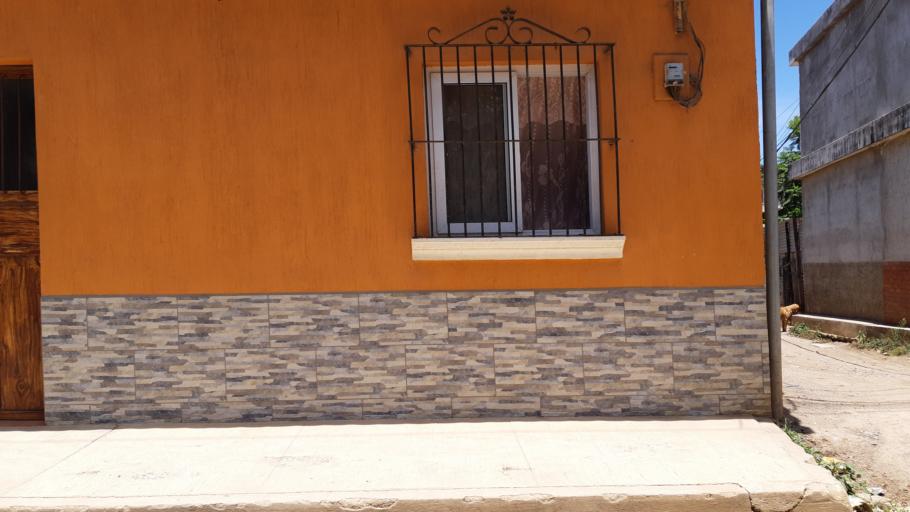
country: GT
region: Chimaltenango
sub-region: Municipio de Chimaltenango
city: Chimaltenango
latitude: 14.6644
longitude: -90.8463
